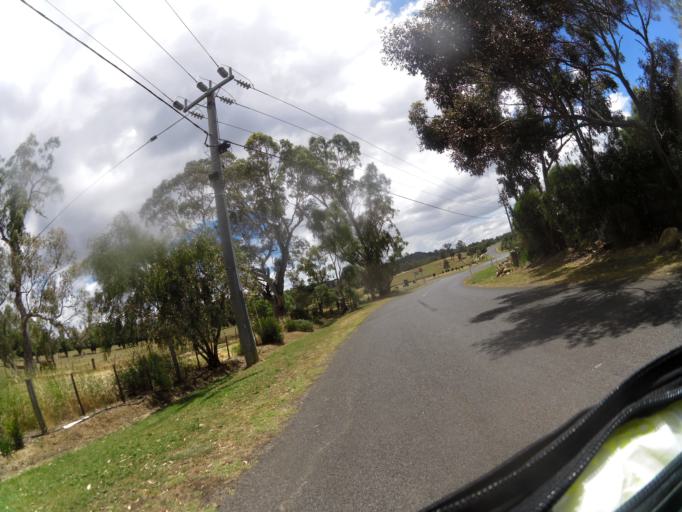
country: AU
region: Victoria
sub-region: Mount Alexander
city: Castlemaine
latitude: -37.0137
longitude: 144.2510
